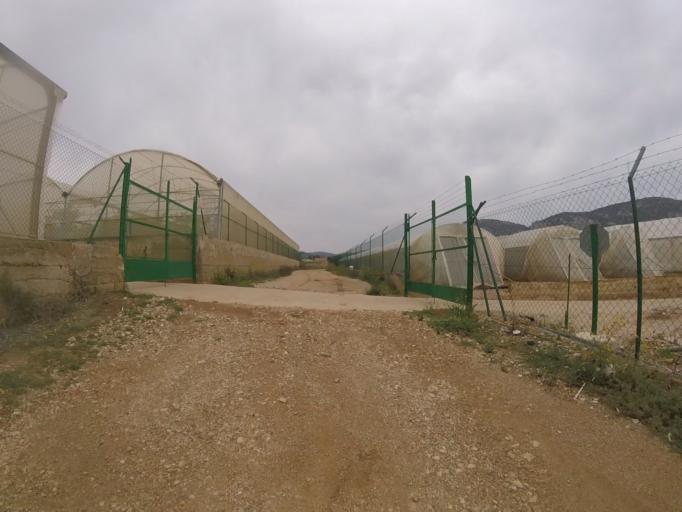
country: ES
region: Valencia
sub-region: Provincia de Castello
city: Alcala de Xivert
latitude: 40.2813
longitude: 0.2551
